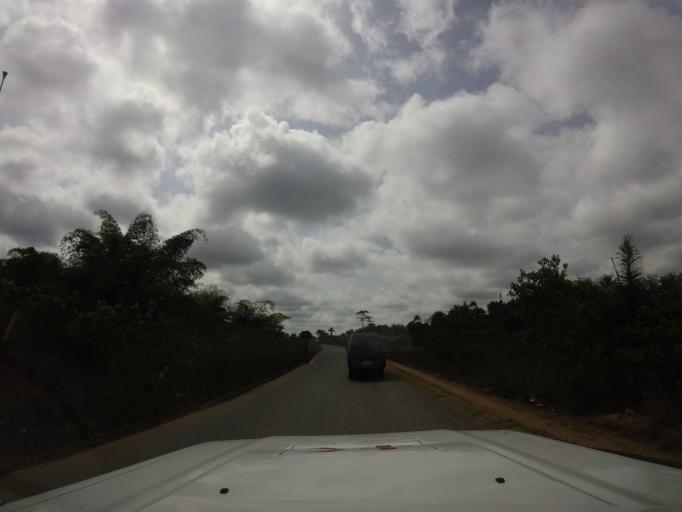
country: LR
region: Montserrado
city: Monrovia
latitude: 6.5061
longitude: -10.8205
